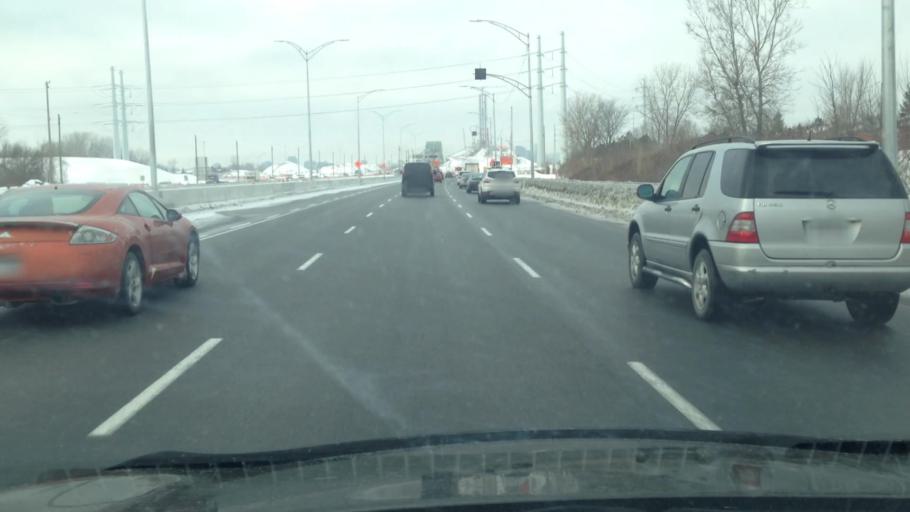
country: CA
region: Quebec
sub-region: Monteregie
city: Brossard
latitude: 45.4656
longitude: -73.4803
